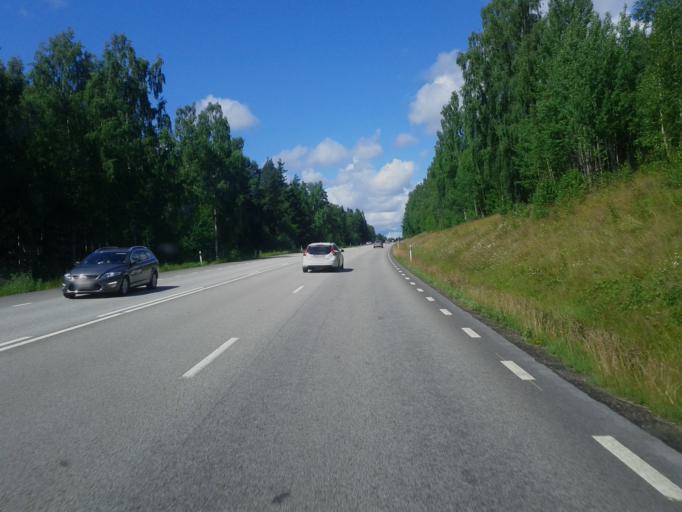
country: SE
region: Dalarna
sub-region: Rattviks Kommun
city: Raettvik
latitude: 60.8983
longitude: 15.0869
